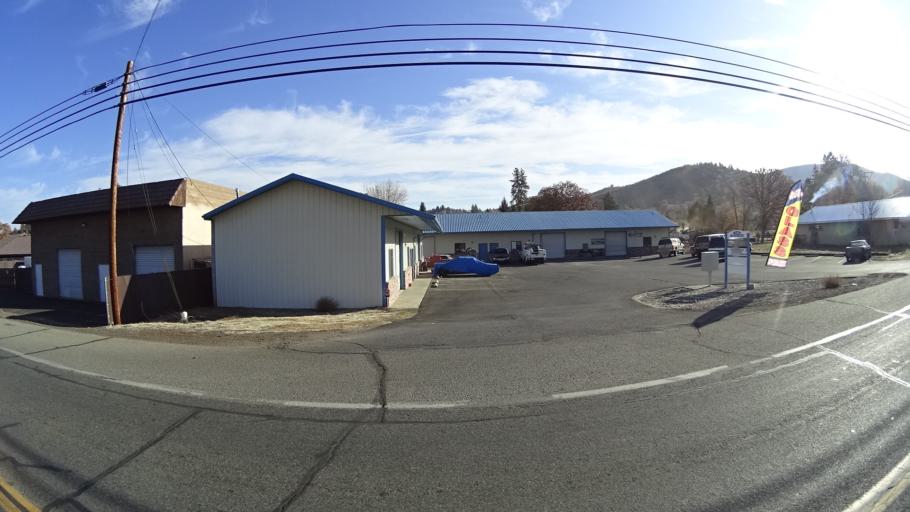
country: US
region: California
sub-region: Siskiyou County
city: Yreka
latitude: 41.6985
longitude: -122.6396
